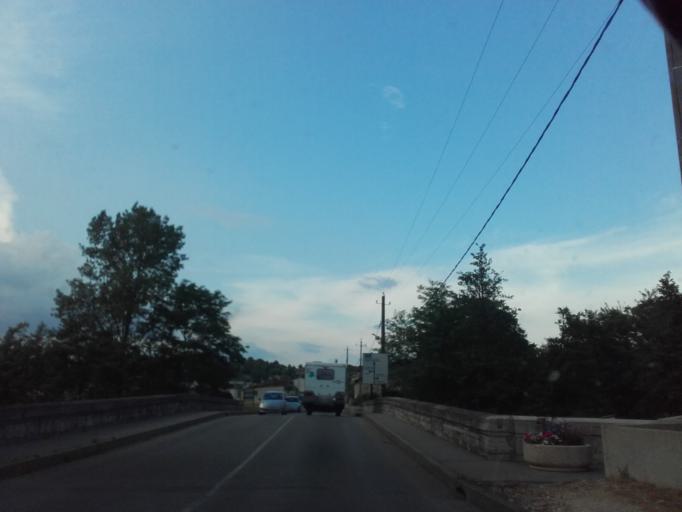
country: FR
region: Rhone-Alpes
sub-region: Departement de l'Isere
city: Auberives-sur-Vareze
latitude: 45.4292
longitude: 4.8172
